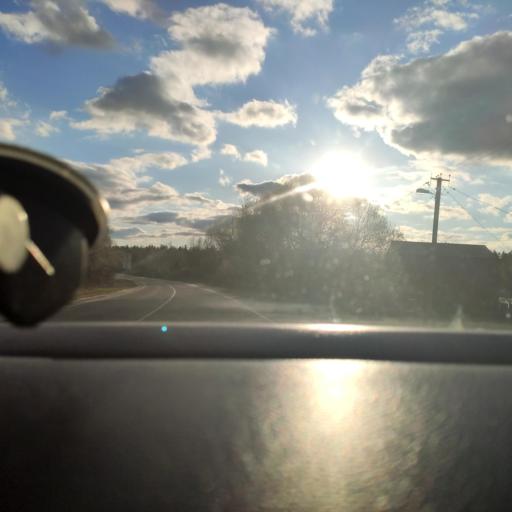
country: RU
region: Moskovskaya
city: Shaturtorf
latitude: 55.4566
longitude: 39.4598
